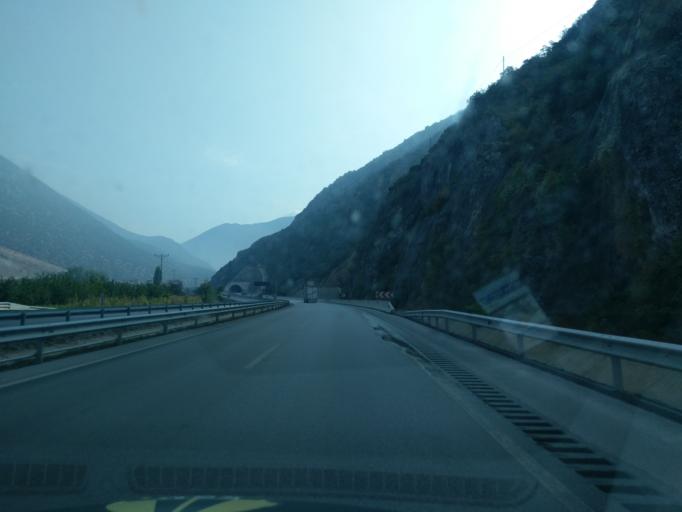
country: TR
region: Amasya
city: Akdag
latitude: 40.6929
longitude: 35.9271
